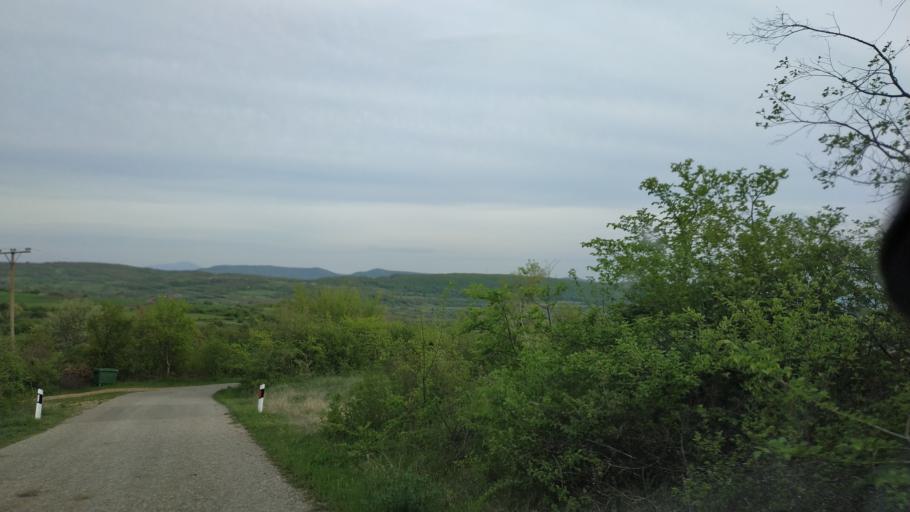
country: RS
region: Central Serbia
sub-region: Zajecarski Okrug
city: Soko Banja
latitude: 43.5313
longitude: 21.8781
